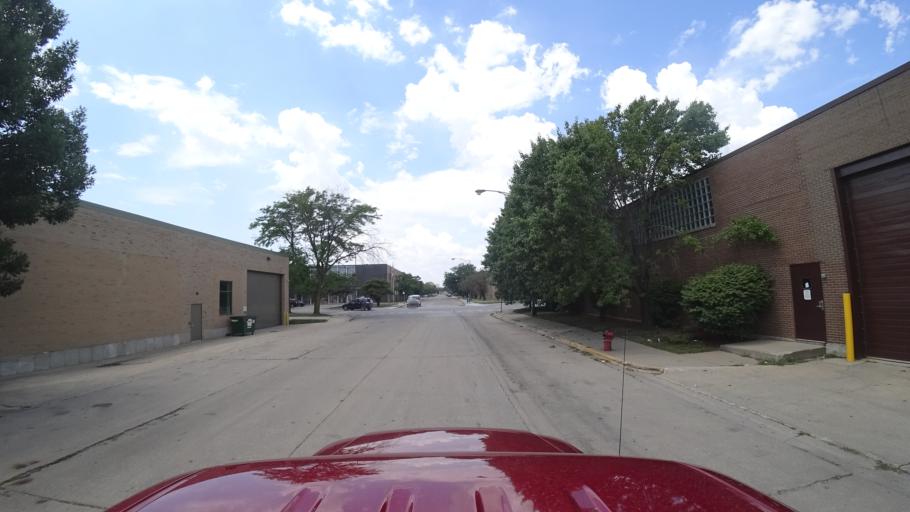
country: US
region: Illinois
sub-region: Cook County
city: Chicago
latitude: 41.8212
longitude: -87.6500
